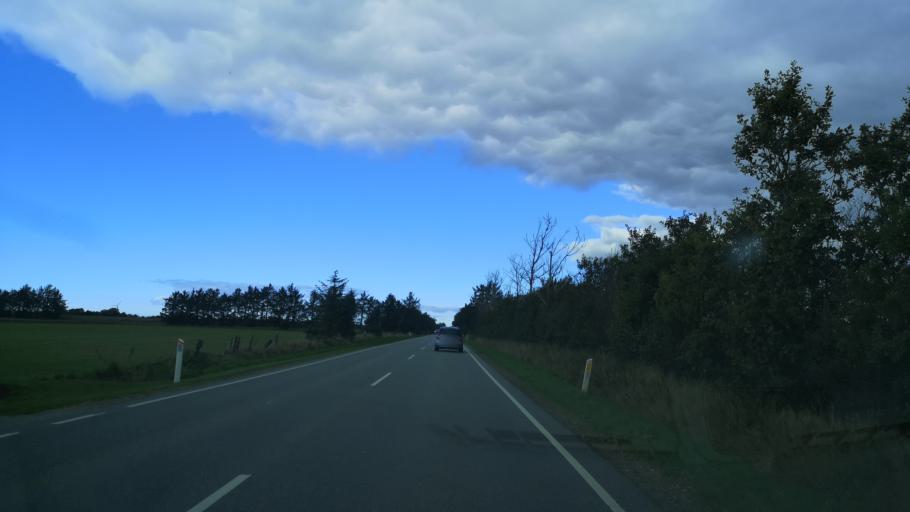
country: DK
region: South Denmark
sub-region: Tonder Kommune
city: Sherrebek
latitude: 55.0720
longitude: 8.8279
